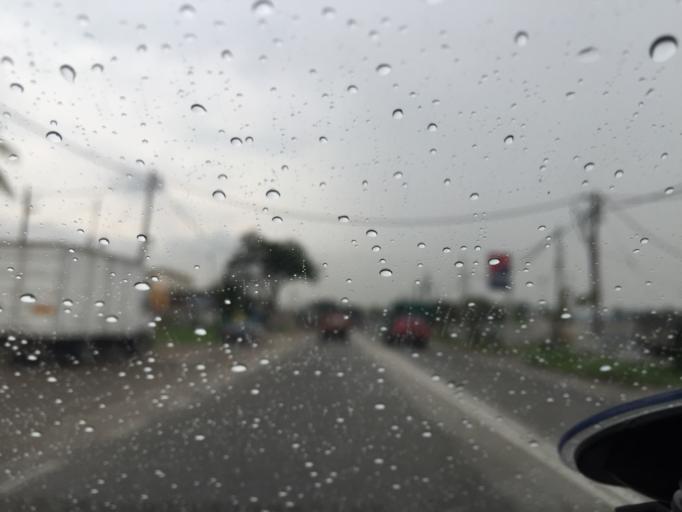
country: MY
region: Selangor
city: Subang Jaya
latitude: 3.0128
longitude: 101.5222
